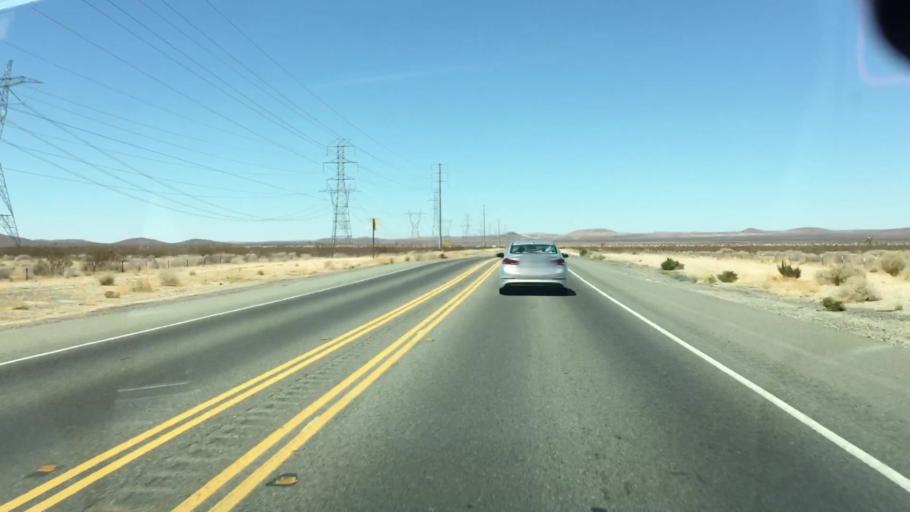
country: US
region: California
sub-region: San Bernardino County
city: Adelanto
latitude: 34.7802
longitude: -117.4806
